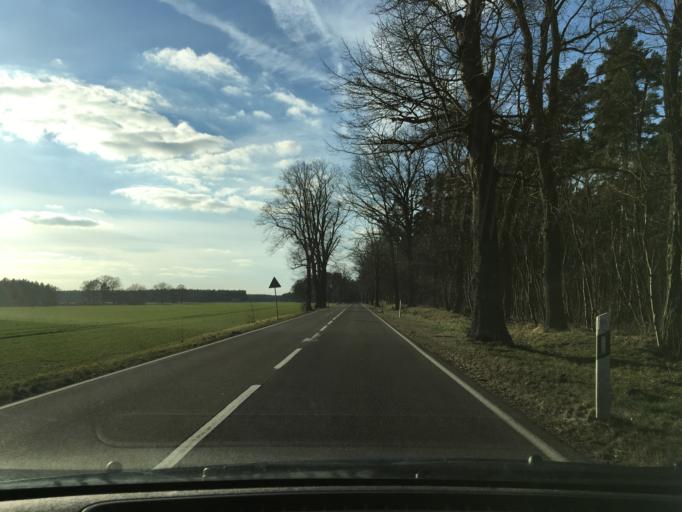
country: DE
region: Saxony-Anhalt
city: Luftkurort Arendsee
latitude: 52.8844
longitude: 11.6063
